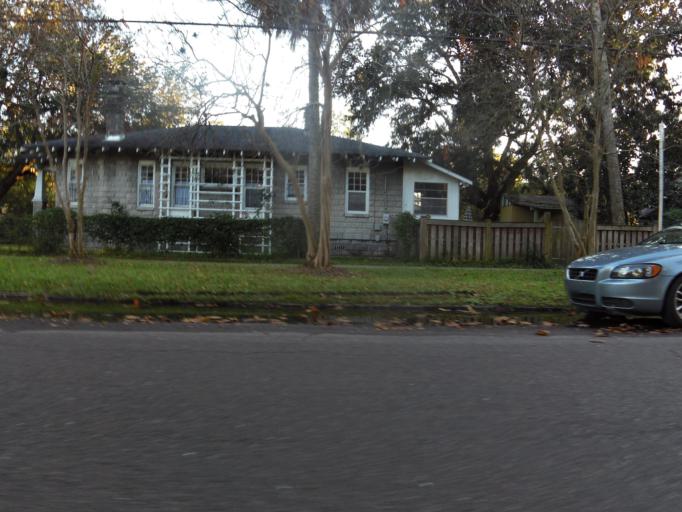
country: US
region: Florida
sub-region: Duval County
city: Jacksonville
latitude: 30.3133
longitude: -81.6930
